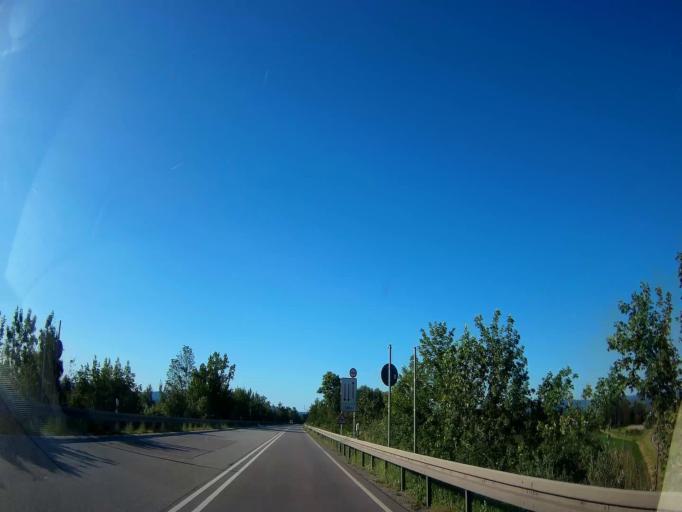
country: DE
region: Bavaria
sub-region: Lower Bavaria
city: Parkstetten
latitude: 48.9041
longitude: 12.6157
